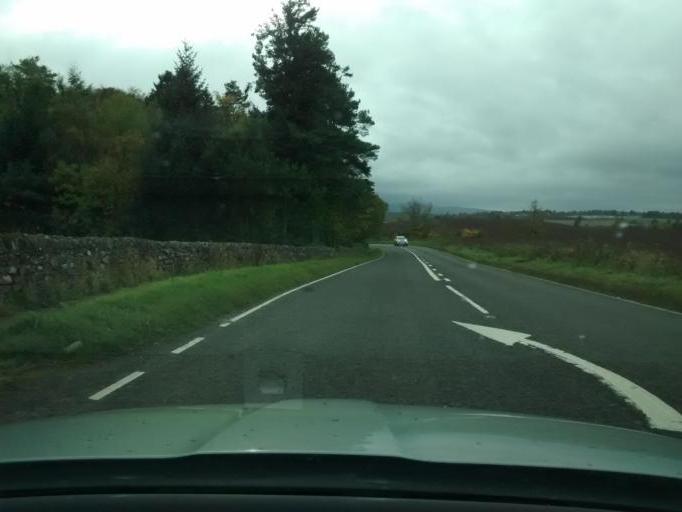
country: GB
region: Scotland
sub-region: Perth and Kinross
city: Auchterarder
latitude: 56.3136
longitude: -3.6700
